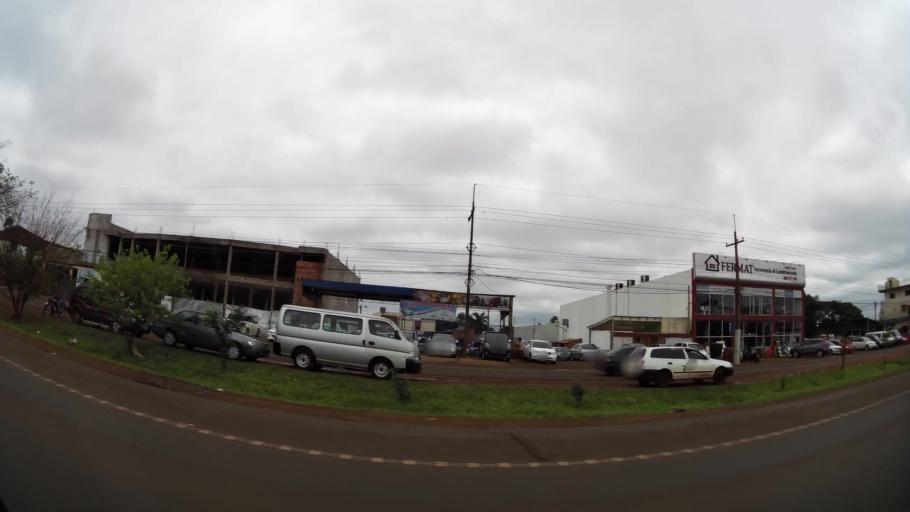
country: PY
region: Alto Parana
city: Ciudad del Este
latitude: -25.4961
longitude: -54.6847
